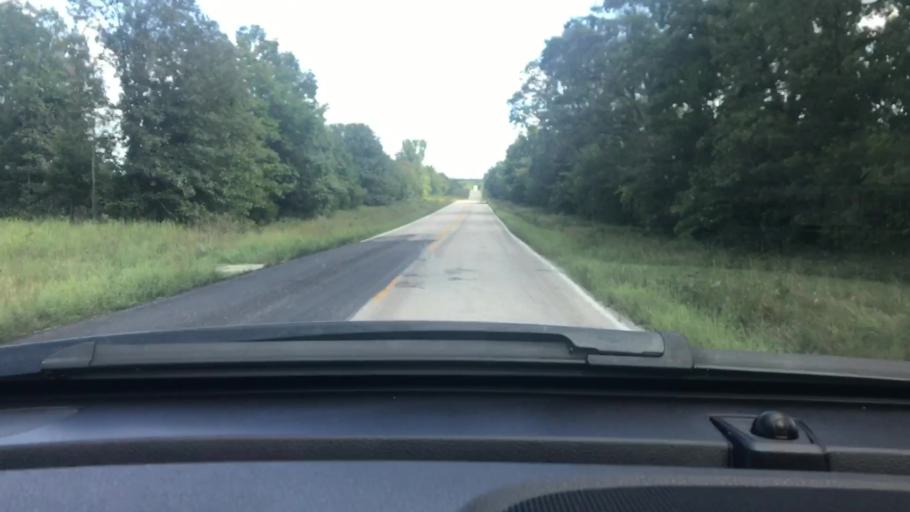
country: US
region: Missouri
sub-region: Wright County
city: Hartville
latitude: 37.3925
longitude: -92.4507
